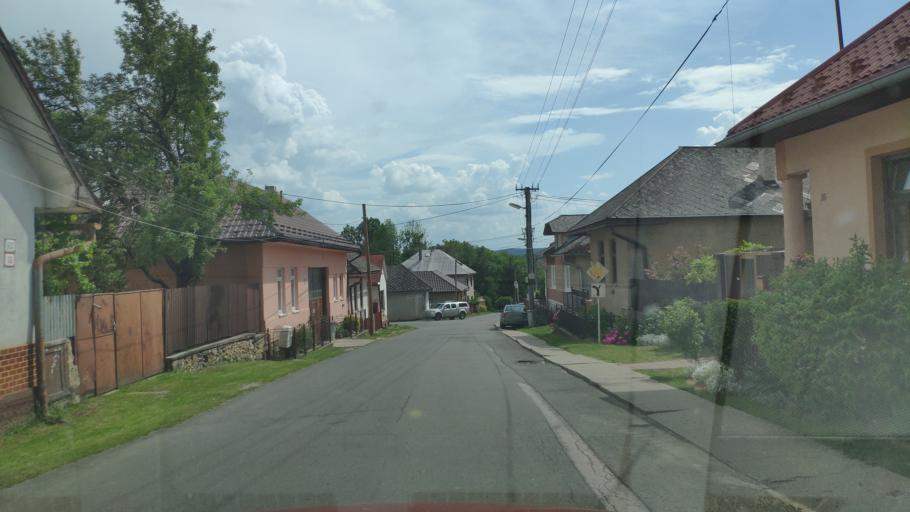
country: SK
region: Kosicky
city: Medzev
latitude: 48.7093
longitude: 20.9743
